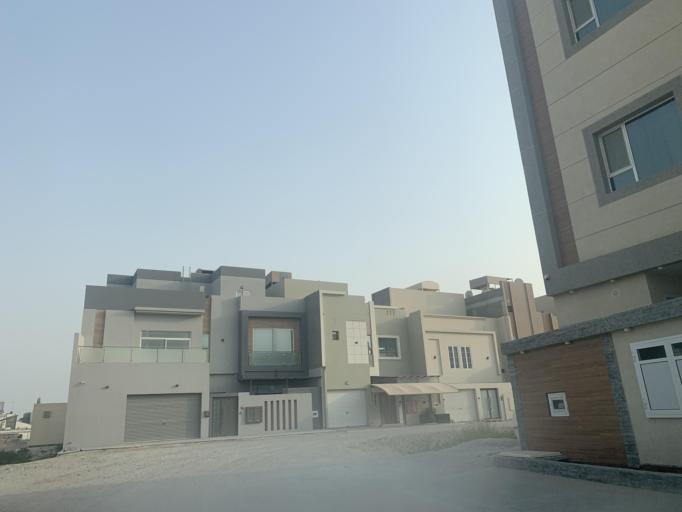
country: BH
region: Manama
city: Jidd Hafs
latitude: 26.2209
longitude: 50.5199
